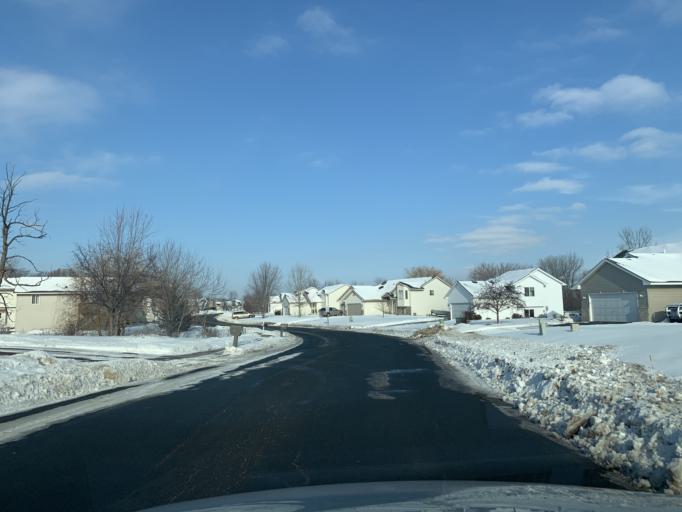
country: US
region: Minnesota
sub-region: Wright County
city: Buffalo
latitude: 45.1945
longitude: -93.8366
